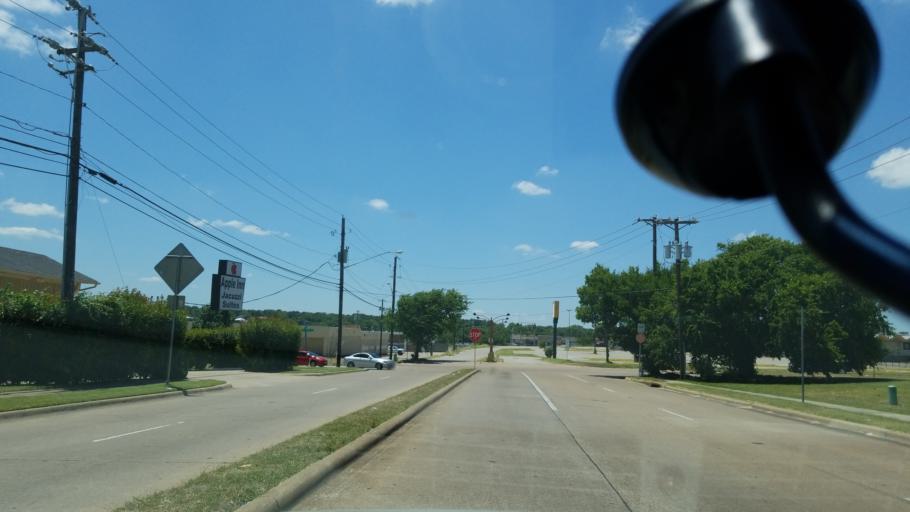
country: US
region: Texas
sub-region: Dallas County
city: Cockrell Hill
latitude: 32.6913
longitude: -96.8242
